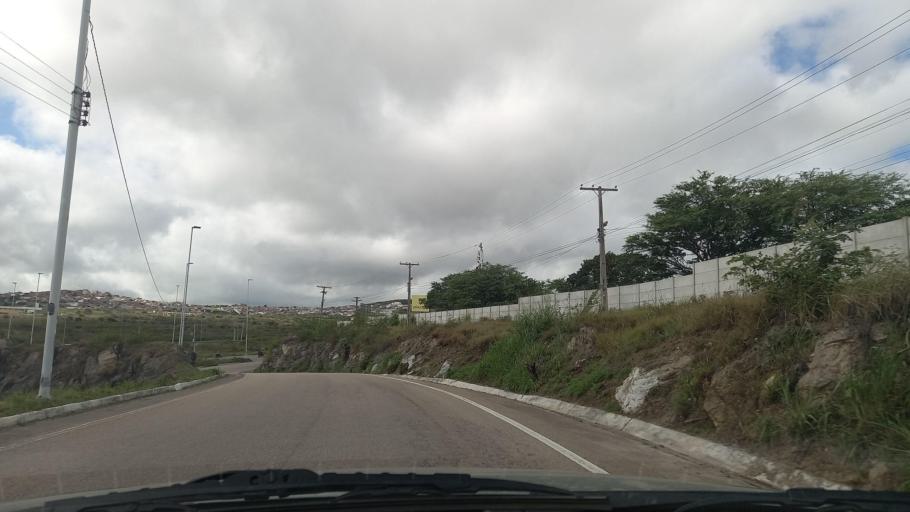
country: BR
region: Pernambuco
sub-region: Caruaru
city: Caruaru
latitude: -8.3008
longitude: -35.9898
